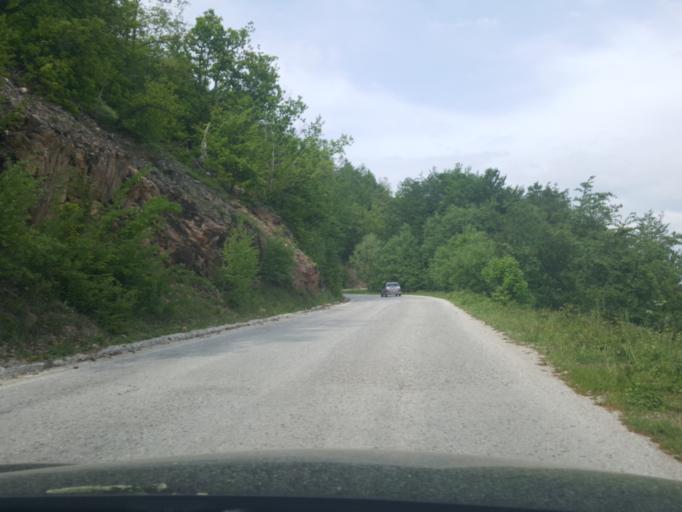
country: RS
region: Central Serbia
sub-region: Zlatiborski Okrug
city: Bajina Basta
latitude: 44.0925
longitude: 19.6597
